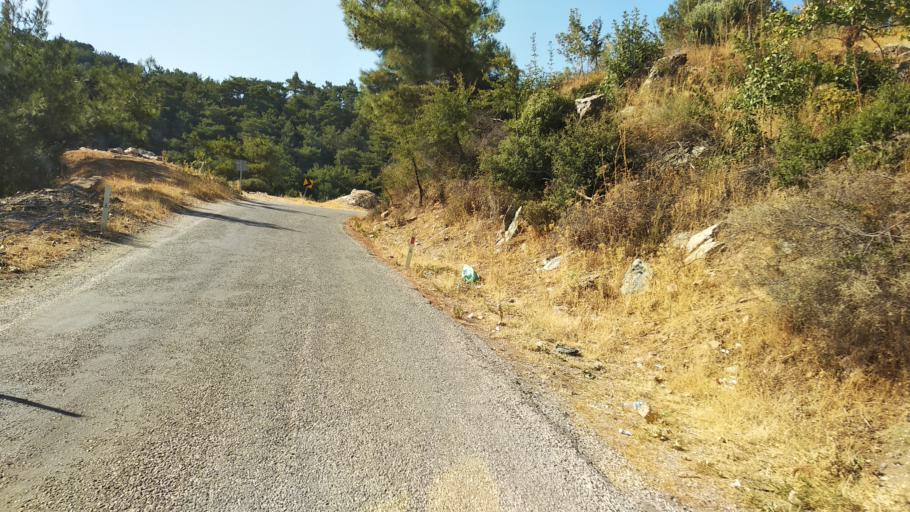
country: TR
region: Izmir
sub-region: Seferihisar
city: Seferhisar
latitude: 38.3196
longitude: 26.9576
